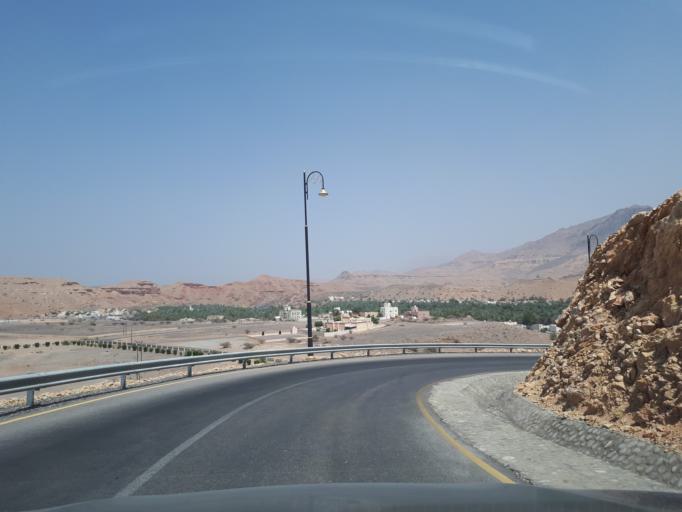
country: OM
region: Ash Sharqiyah
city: Ibra'
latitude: 23.0900
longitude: 58.8500
